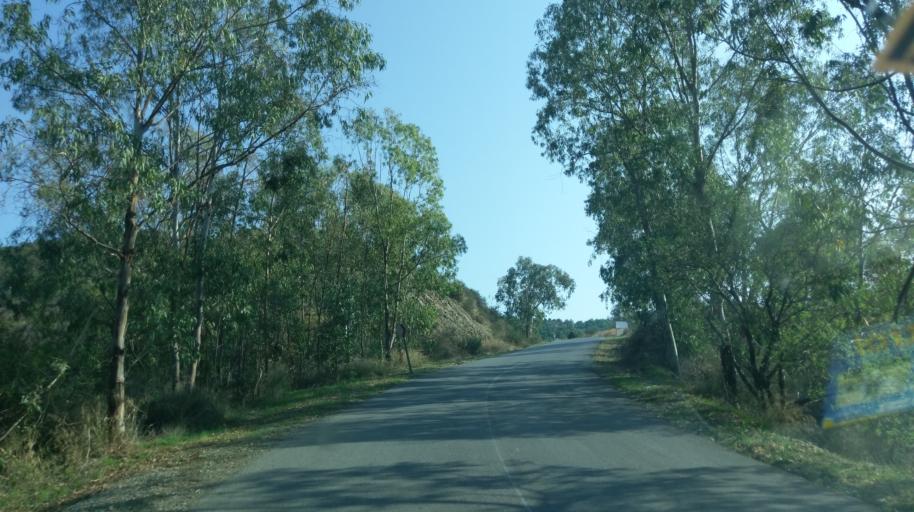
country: CY
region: Lefkosia
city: Kato Pyrgos
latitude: 35.1646
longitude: 32.7490
